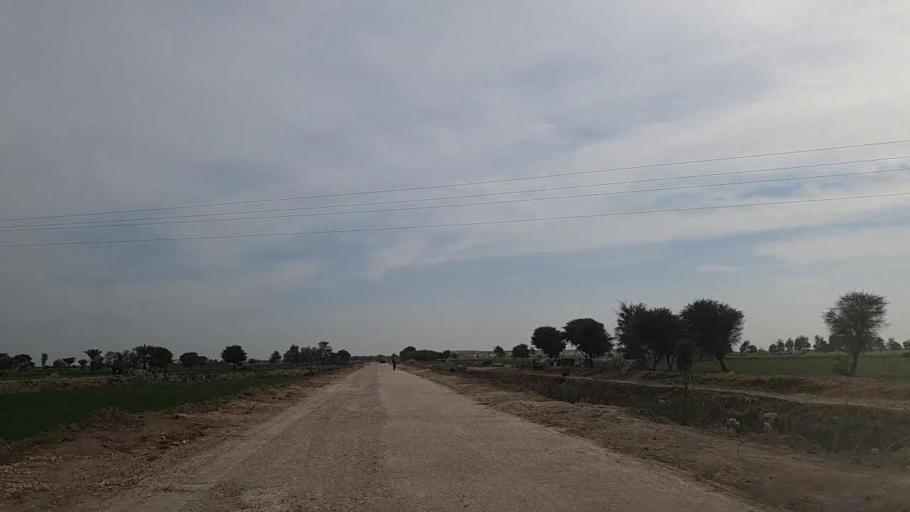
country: PK
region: Sindh
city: Jam Sahib
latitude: 26.4091
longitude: 68.4927
